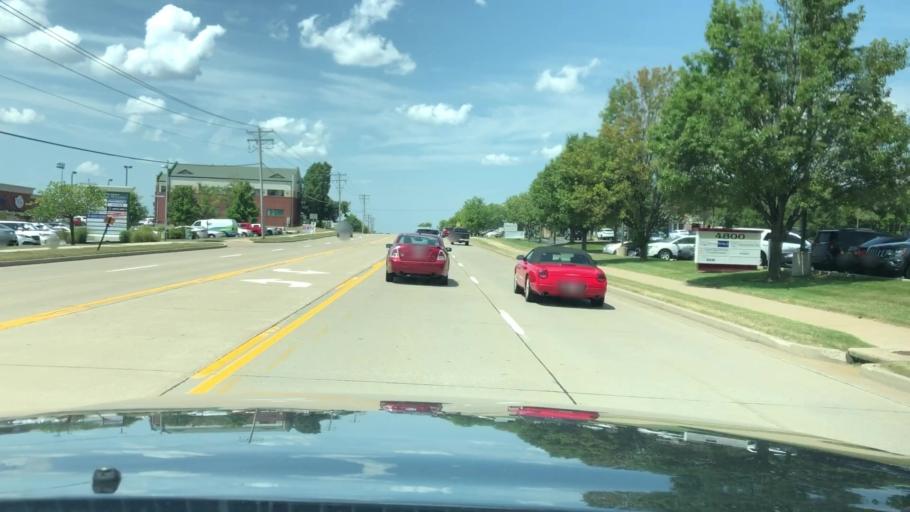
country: US
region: Missouri
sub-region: Saint Charles County
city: Saint Peters
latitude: 38.7924
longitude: -90.5868
